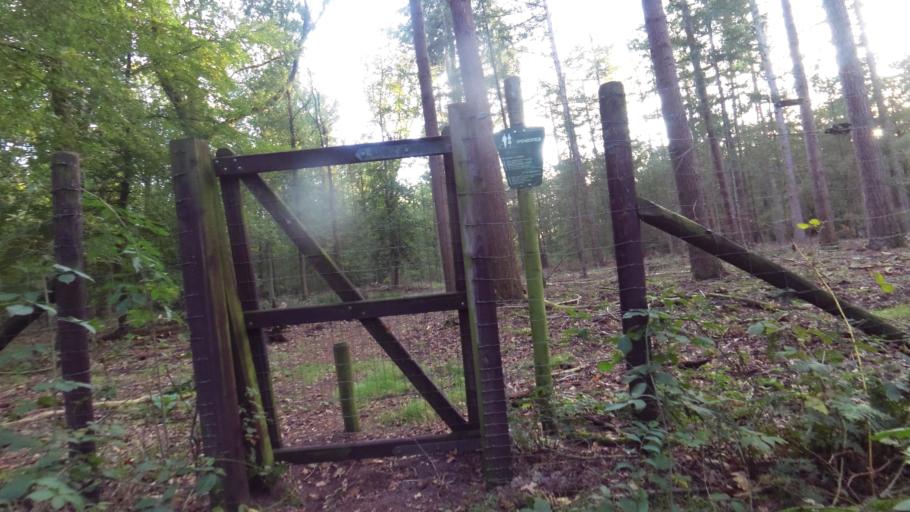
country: NL
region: Gelderland
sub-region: Gemeente Nunspeet
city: Nunspeet
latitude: 52.3216
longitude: 5.8282
